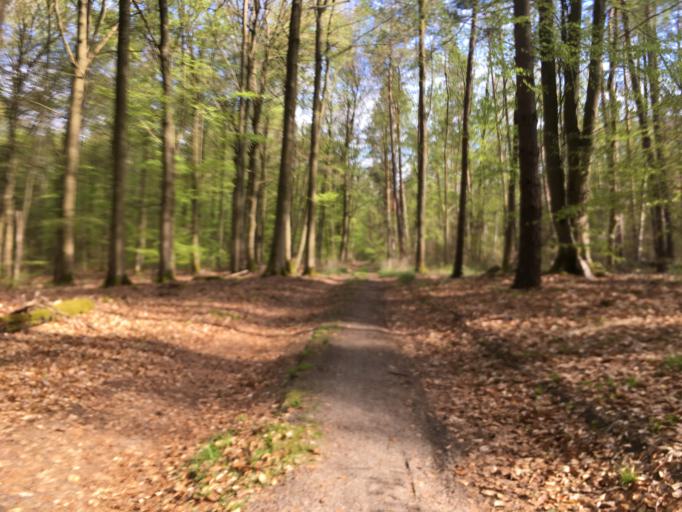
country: DE
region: Brandenburg
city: Bernau bei Berlin
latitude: 52.7245
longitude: 13.5584
